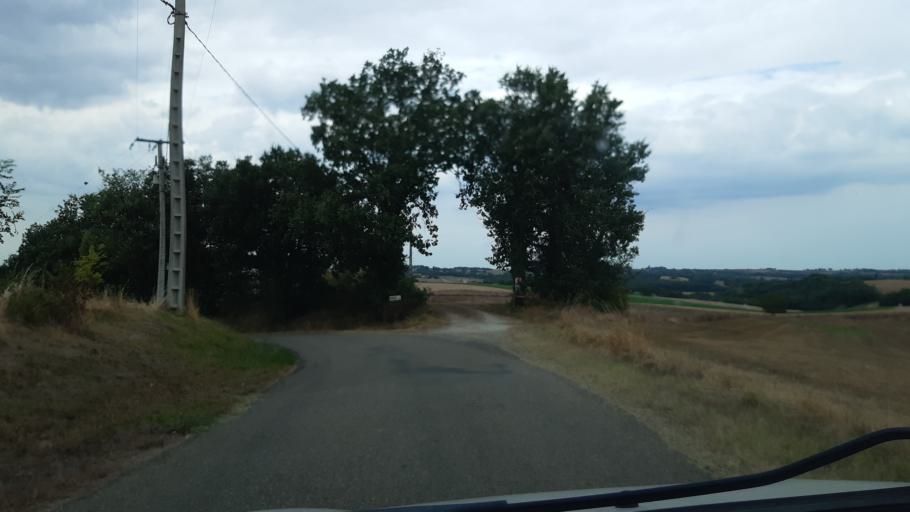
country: FR
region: Midi-Pyrenees
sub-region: Departement du Gers
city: Gimont
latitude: 43.7007
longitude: 0.9885
